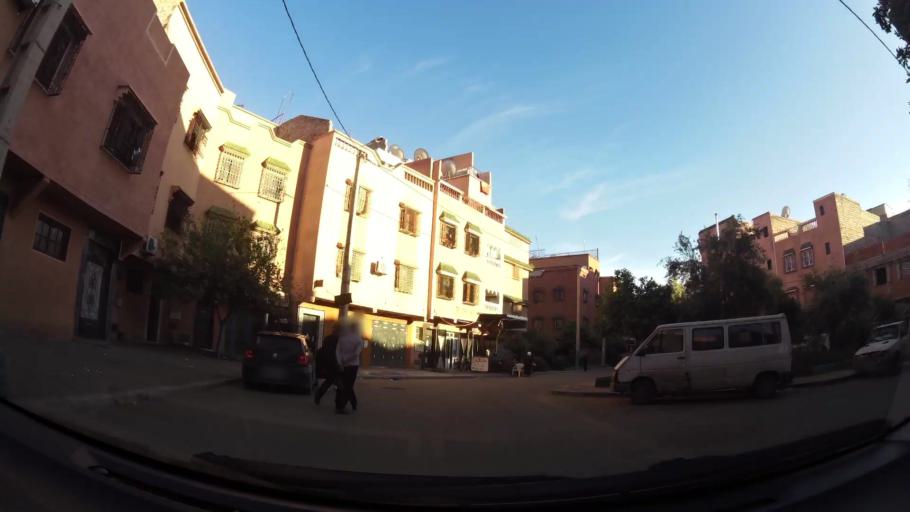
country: MA
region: Marrakech-Tensift-Al Haouz
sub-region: Marrakech
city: Marrakesh
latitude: 31.6186
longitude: -8.0512
